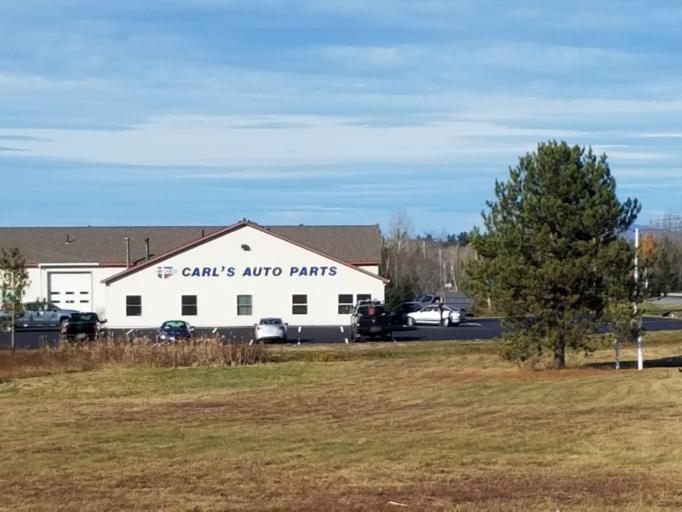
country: US
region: Maine
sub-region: Penobscot County
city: Lincoln
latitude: 45.3539
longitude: -68.5328
